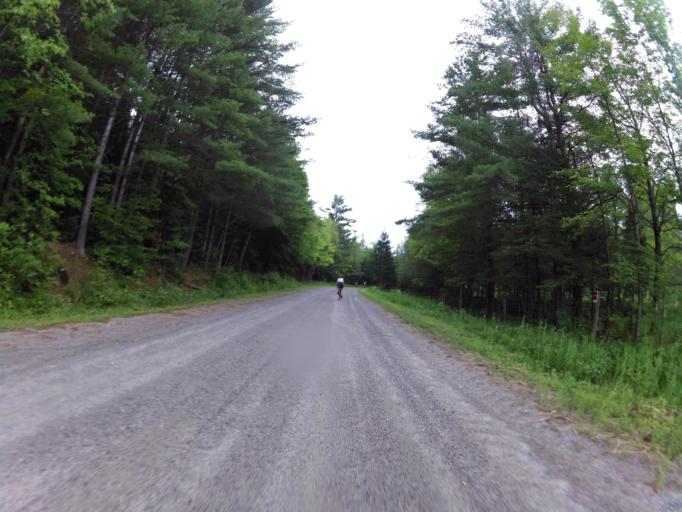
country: CA
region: Ontario
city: Renfrew
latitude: 45.1168
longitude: -76.6230
